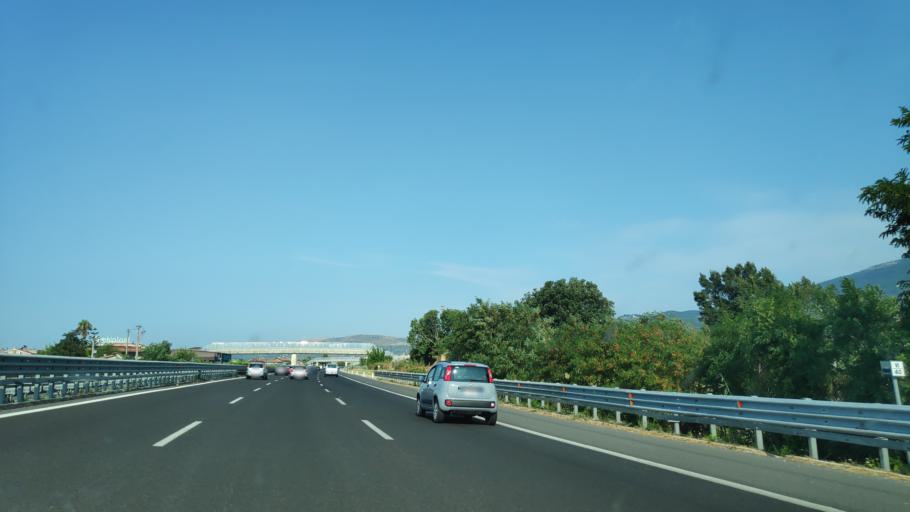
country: IT
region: Campania
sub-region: Provincia di Salerno
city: Quadrivio
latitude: 40.6062
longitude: 15.1020
